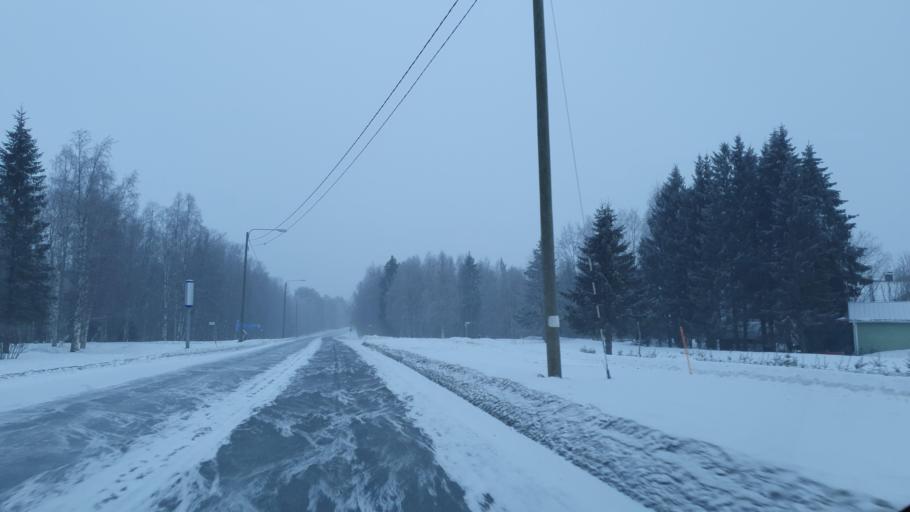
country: FI
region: Lapland
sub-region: Kemi-Tornio
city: Tornio
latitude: 65.9735
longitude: 24.0629
